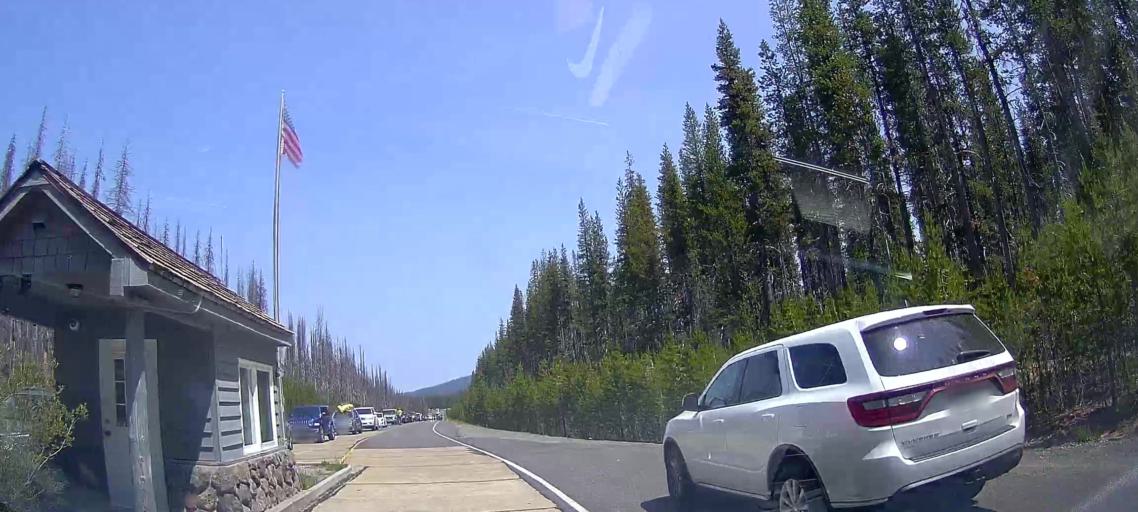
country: US
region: Oregon
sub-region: Lane County
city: Oakridge
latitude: 43.0776
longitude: -122.1180
